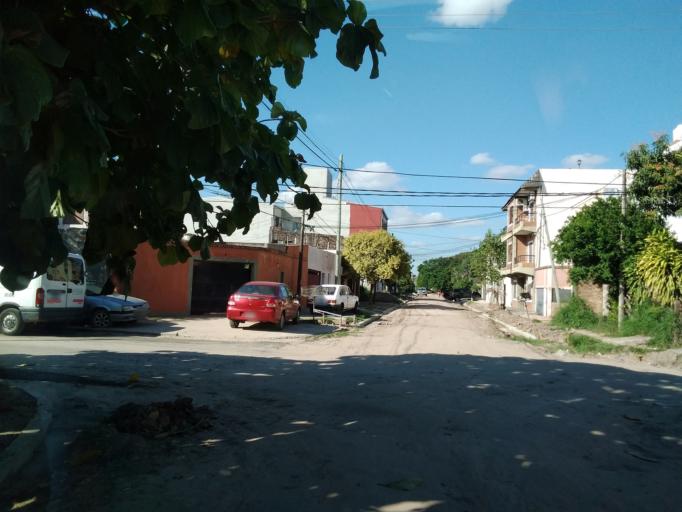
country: AR
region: Corrientes
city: Corrientes
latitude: -27.4639
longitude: -58.7821
